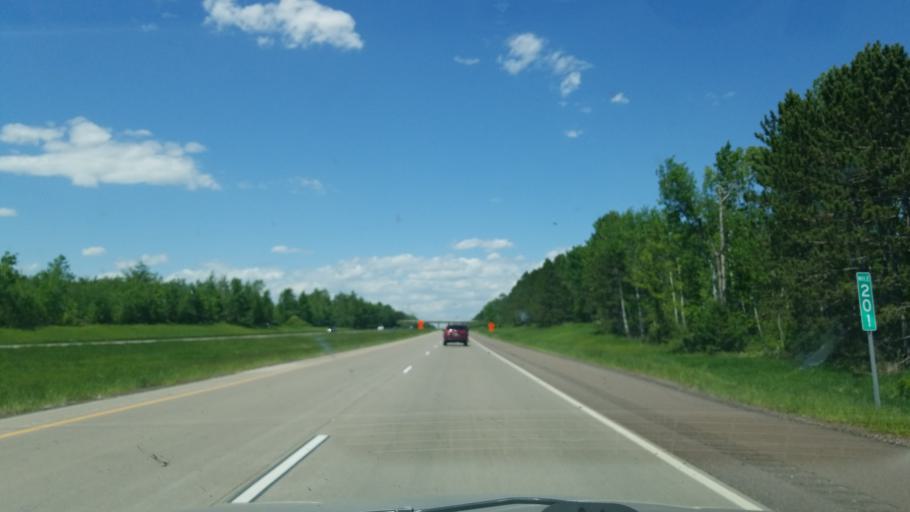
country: US
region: Minnesota
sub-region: Pine County
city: Sandstone
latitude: 46.2537
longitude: -92.8251
